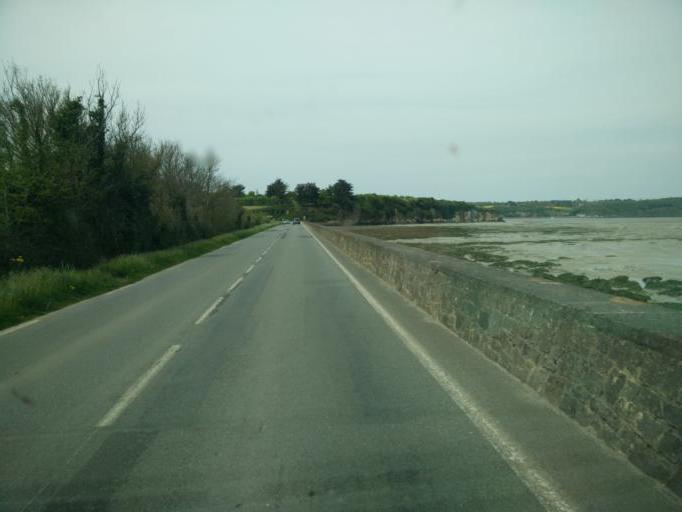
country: FR
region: Brittany
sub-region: Departement des Cotes-d'Armor
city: Matignon
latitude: 48.6114
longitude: -2.3178
